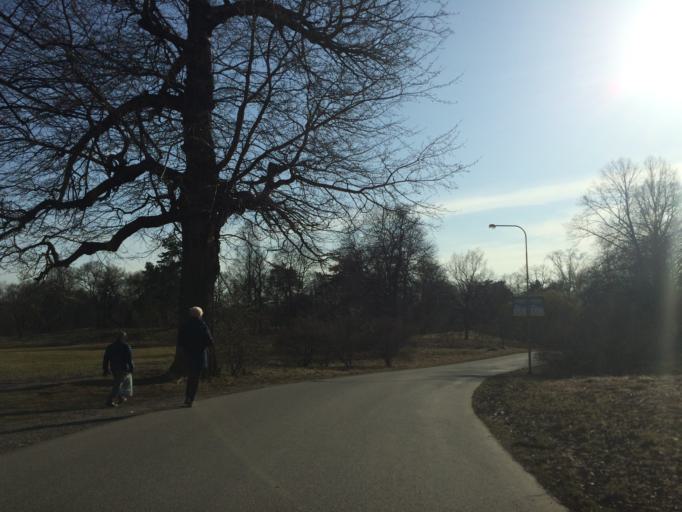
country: SE
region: Stockholm
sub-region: Stockholms Kommun
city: OEstermalm
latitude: 59.3261
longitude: 18.1169
